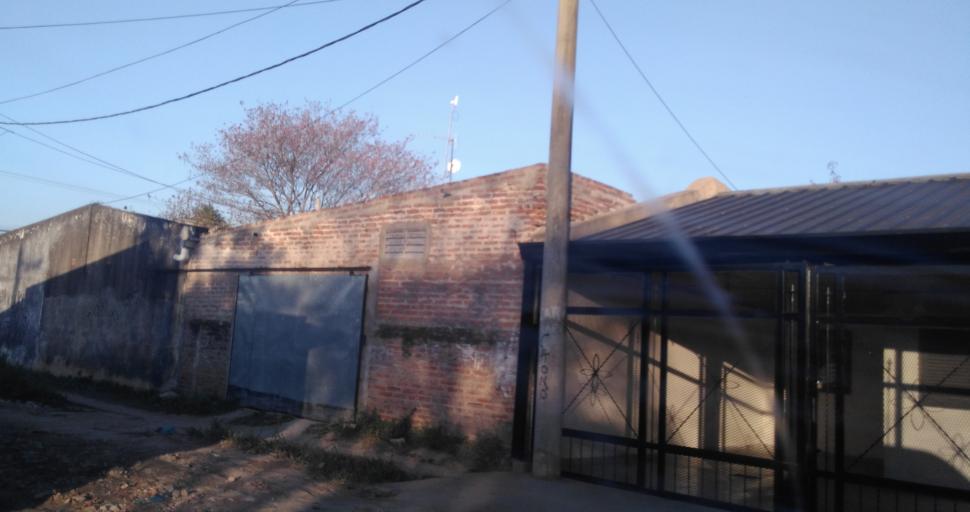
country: AR
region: Chaco
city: Fontana
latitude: -27.4244
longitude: -59.0248
